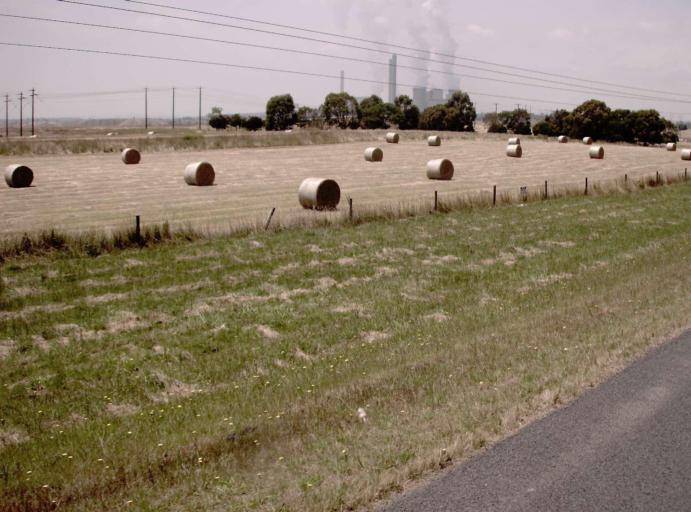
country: AU
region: Victoria
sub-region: Latrobe
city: Traralgon
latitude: -38.2330
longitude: 146.5408
